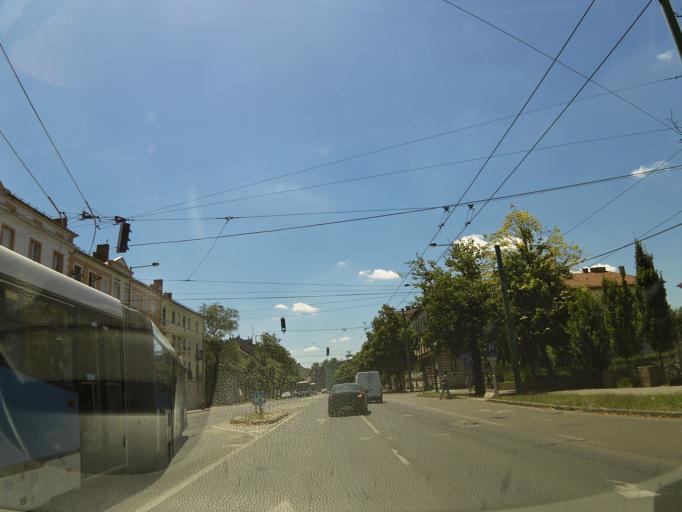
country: HU
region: Csongrad
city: Szeged
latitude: 46.2562
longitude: 20.1409
